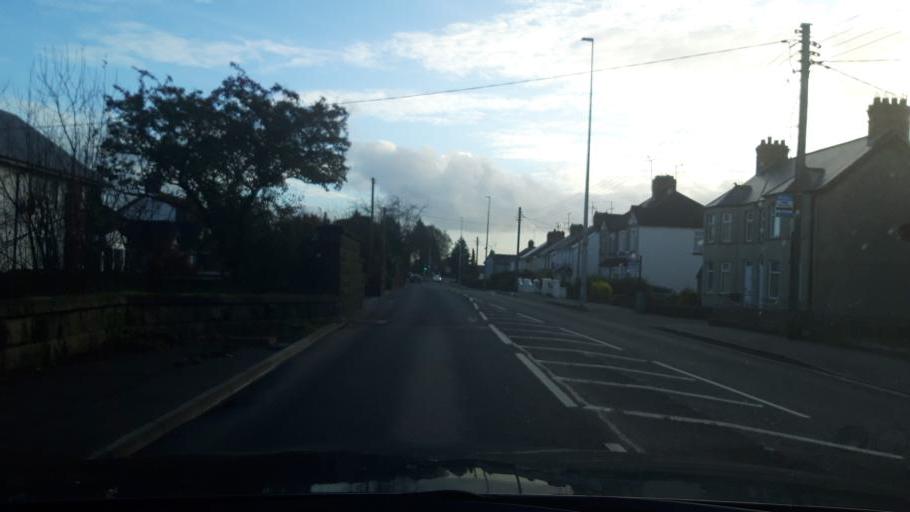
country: GB
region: Northern Ireland
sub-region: Dungannon District
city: Dungannon
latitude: 54.5002
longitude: -6.7630
